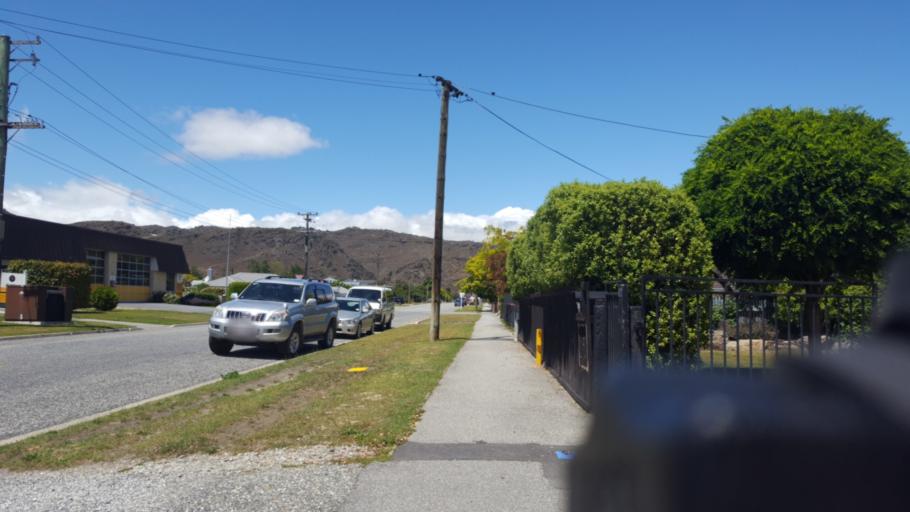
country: NZ
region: Otago
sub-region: Queenstown-Lakes District
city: Wanaka
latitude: -45.2501
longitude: 169.3906
